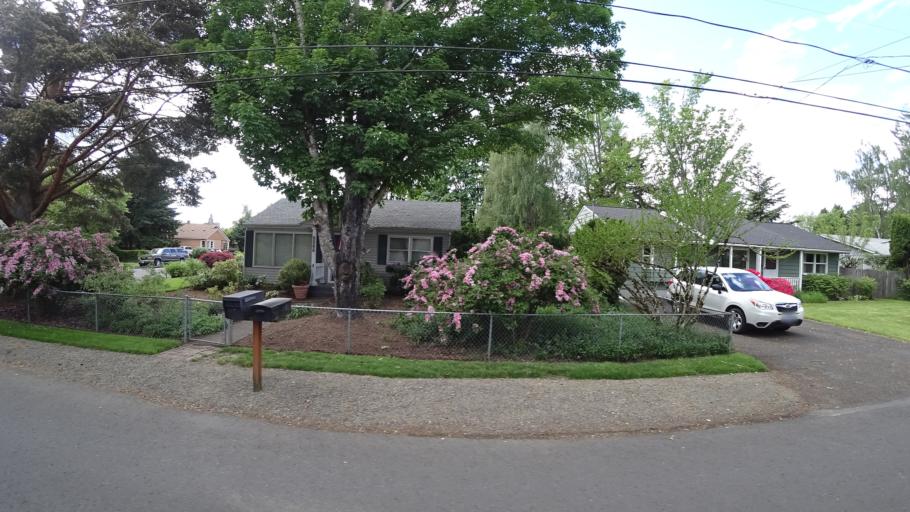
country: US
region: Oregon
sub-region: Washington County
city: Beaverton
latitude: 45.4831
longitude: -122.8201
